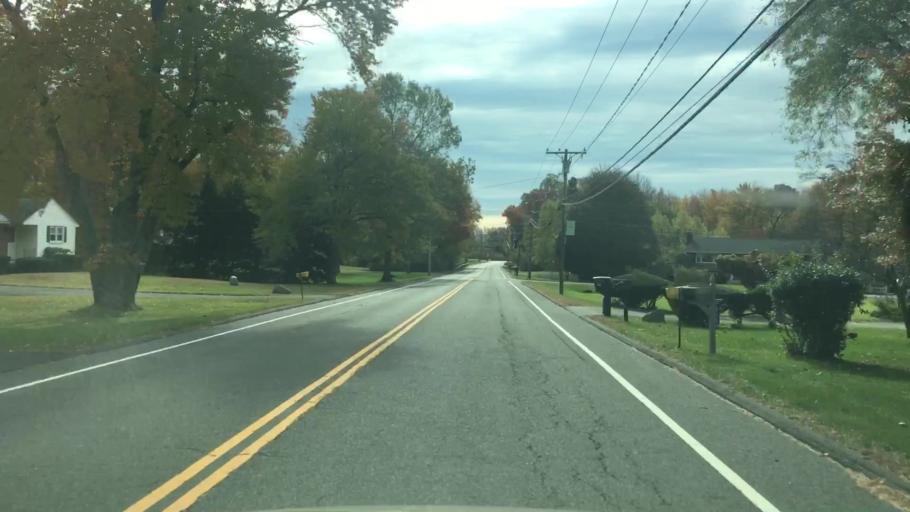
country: US
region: Connecticut
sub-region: Tolland County
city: Somers
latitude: 42.0147
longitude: -72.4830
